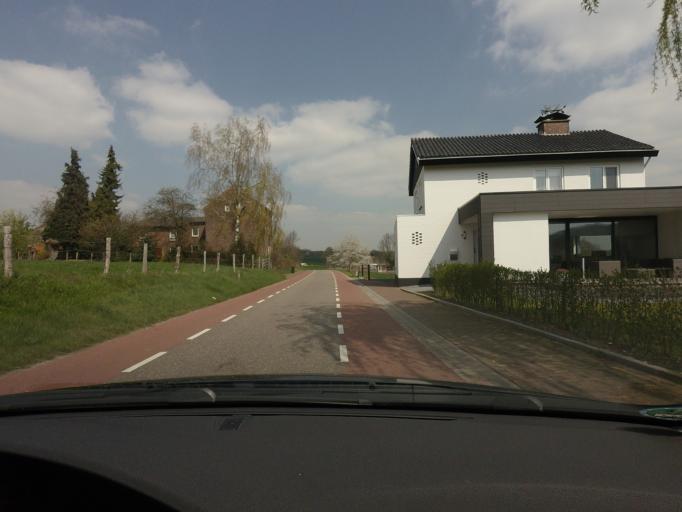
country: NL
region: Limburg
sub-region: Eijsden-Margraten
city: Margraten
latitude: 50.7942
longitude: 5.8603
